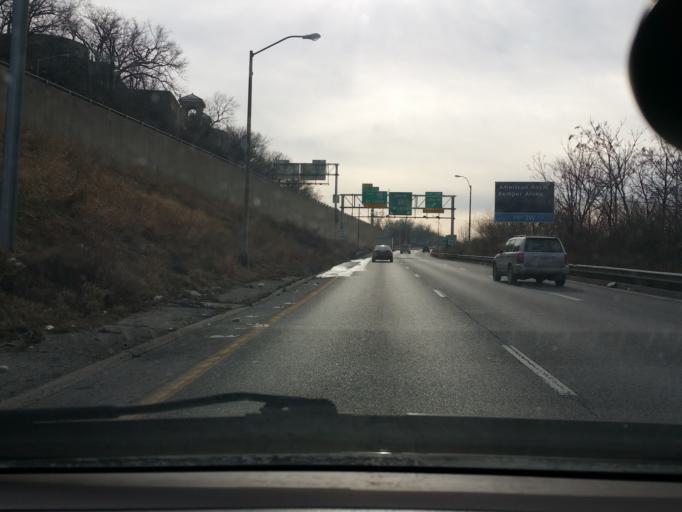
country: US
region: Missouri
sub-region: Jackson County
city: Kansas City
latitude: 39.1040
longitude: -94.5935
